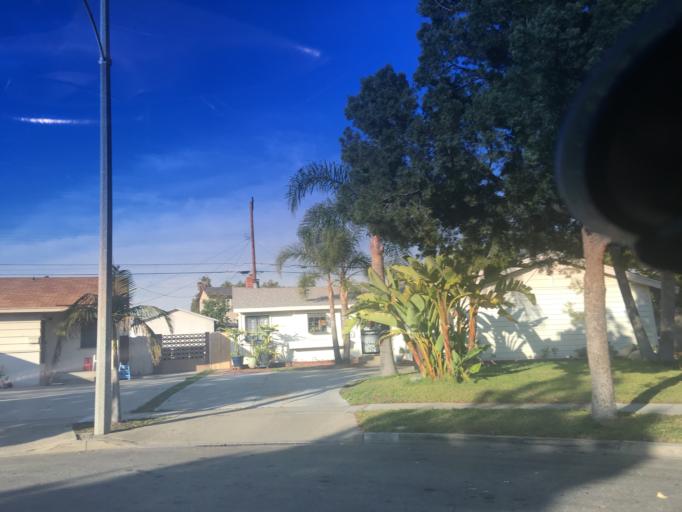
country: US
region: California
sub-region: Orange County
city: Anaheim
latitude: 33.8230
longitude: -117.8937
